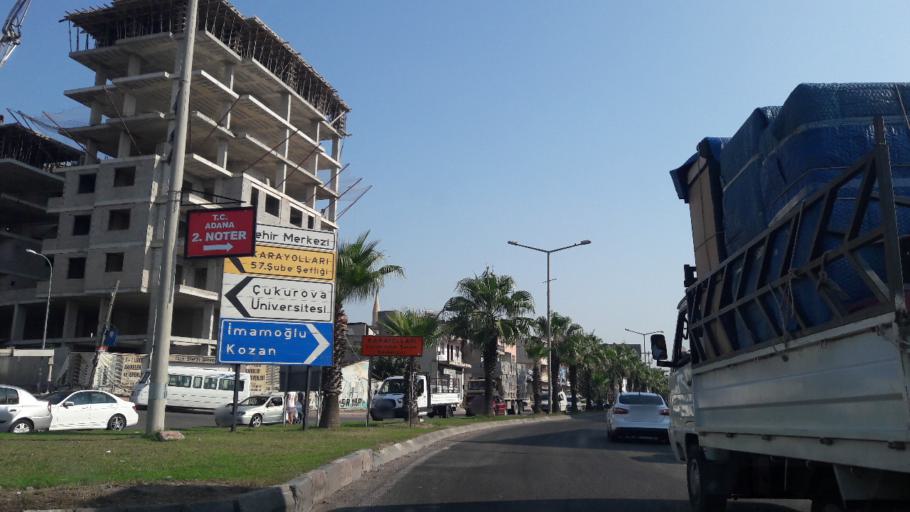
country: TR
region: Adana
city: Yuregir
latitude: 37.0254
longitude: 35.3996
